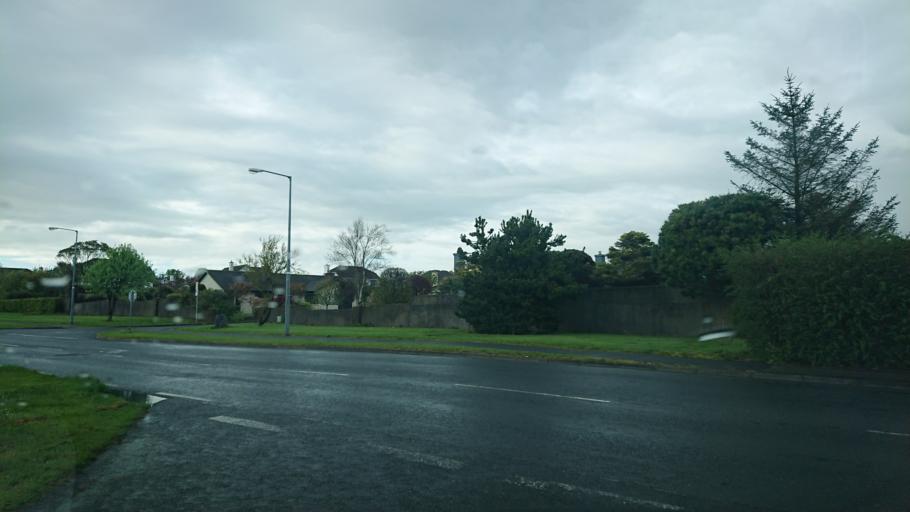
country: IE
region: Munster
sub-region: Waterford
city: Waterford
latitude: 52.2358
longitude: -7.0792
